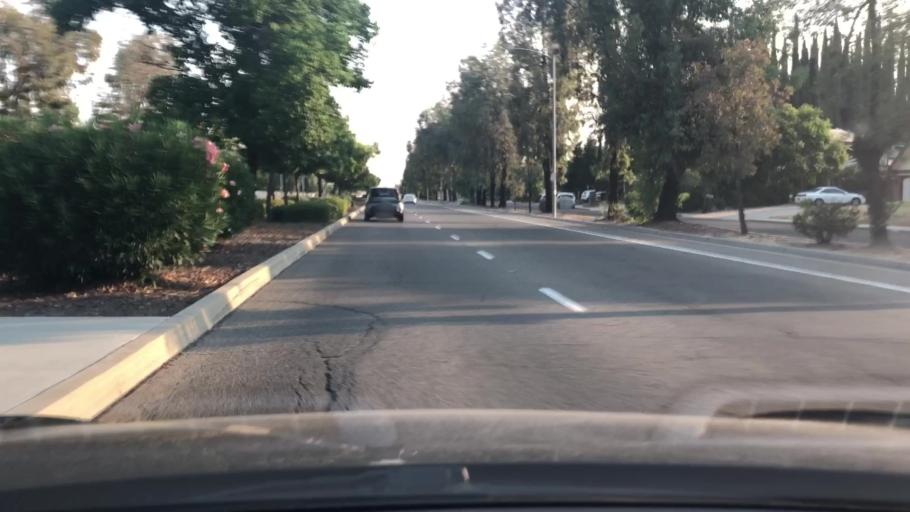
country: US
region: California
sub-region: Fresno County
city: Clovis
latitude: 36.8314
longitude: -119.7295
